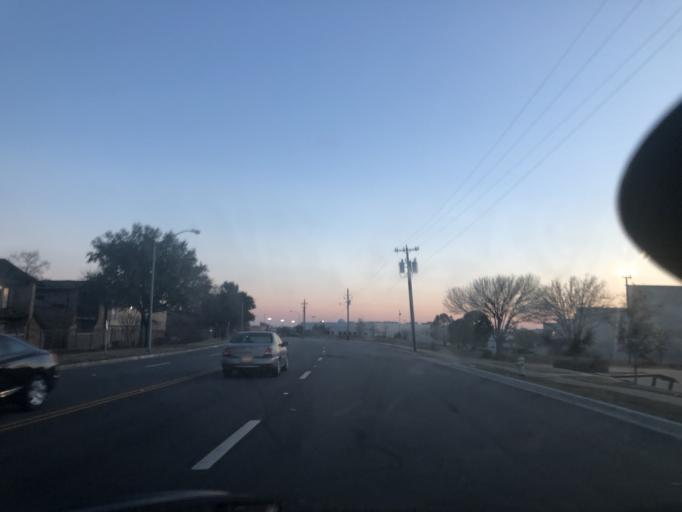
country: US
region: Texas
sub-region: Tarrant County
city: White Settlement
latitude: 32.7292
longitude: -97.4793
